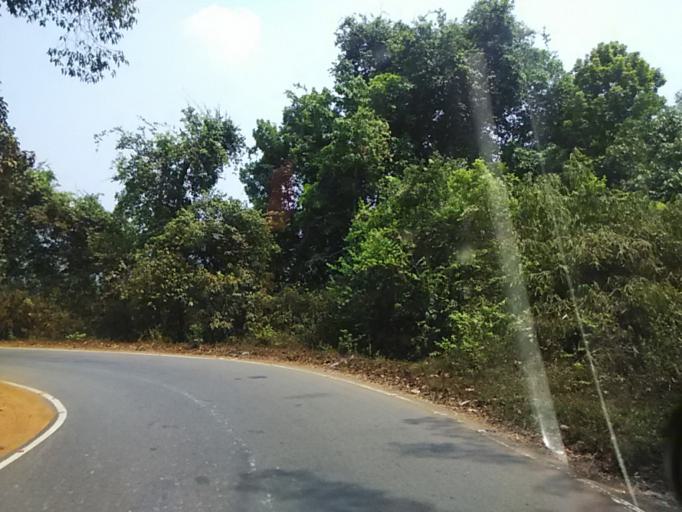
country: IN
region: Karnataka
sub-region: Kodagu
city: Virarajendrapet
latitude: 12.0796
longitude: 75.7352
